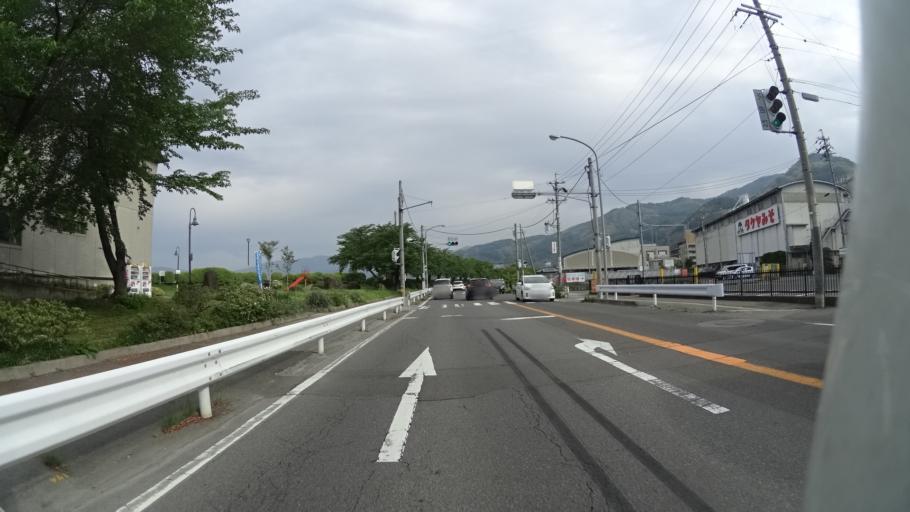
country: JP
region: Nagano
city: Suwa
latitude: 36.0537
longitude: 138.1124
